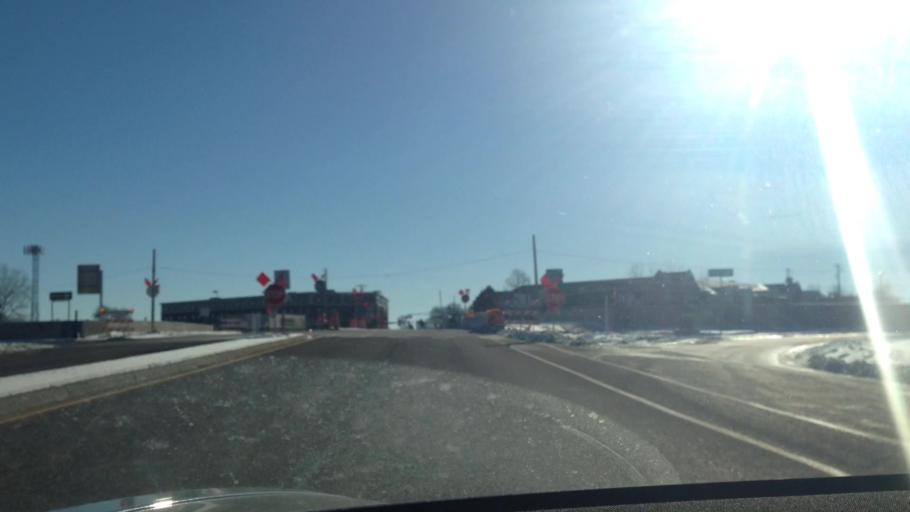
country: US
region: Minnesota
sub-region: Hennepin County
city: Saint Louis Park
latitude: 44.9396
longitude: -93.3572
